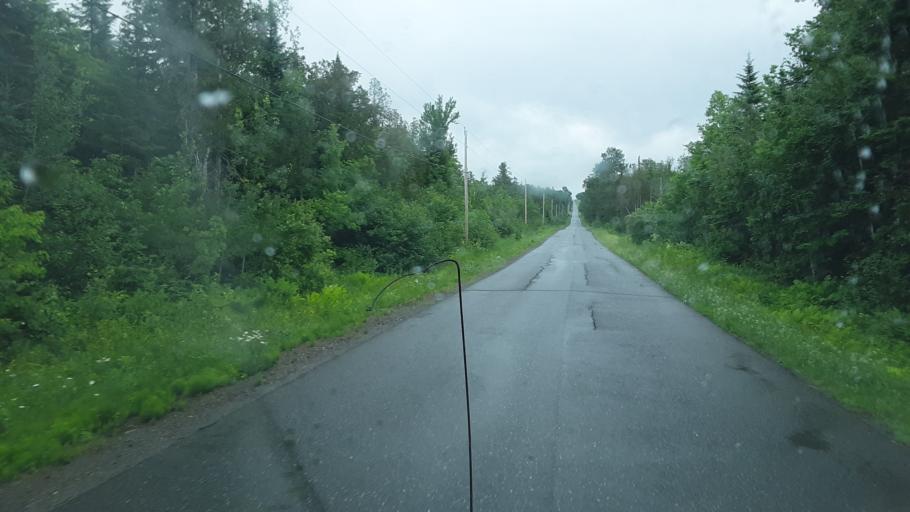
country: US
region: Maine
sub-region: Aroostook County
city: Presque Isle
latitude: 46.6814
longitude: -68.2065
